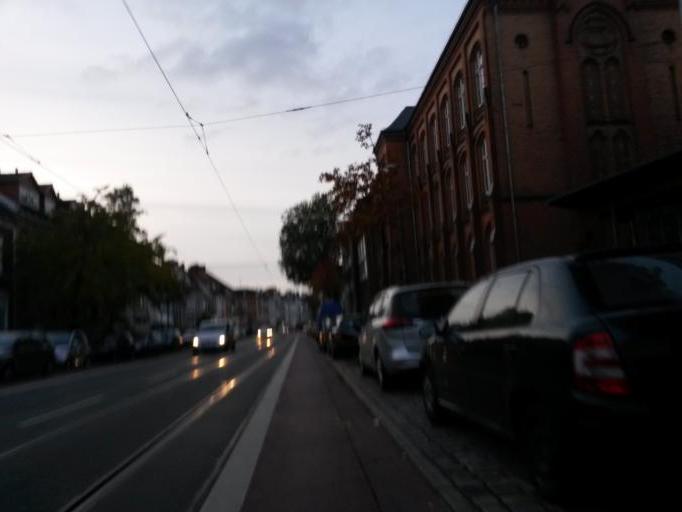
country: DE
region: Bremen
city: Bremen
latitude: 53.0702
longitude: 8.8358
